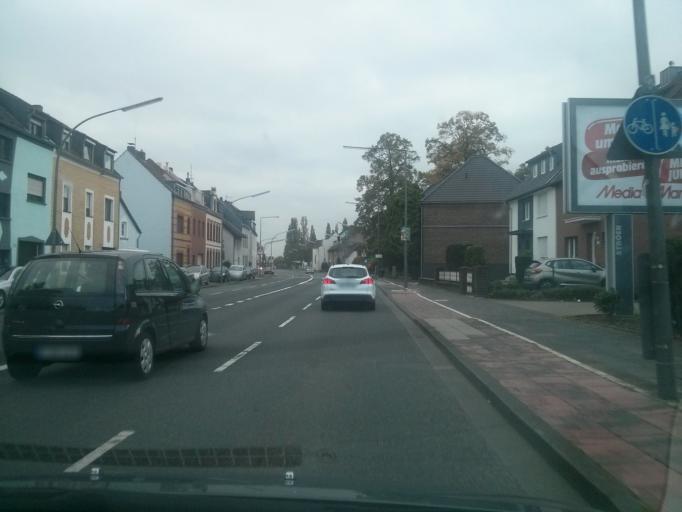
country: DE
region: North Rhine-Westphalia
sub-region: Regierungsbezirk Koln
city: Porz am Rhein
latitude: 50.8981
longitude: 7.0339
